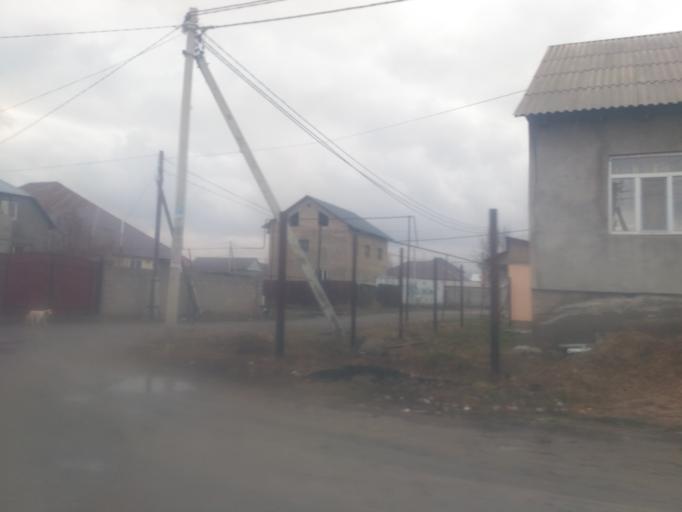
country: KZ
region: Almaty Oblysy
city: Burunday
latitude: 43.2168
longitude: 76.7499
